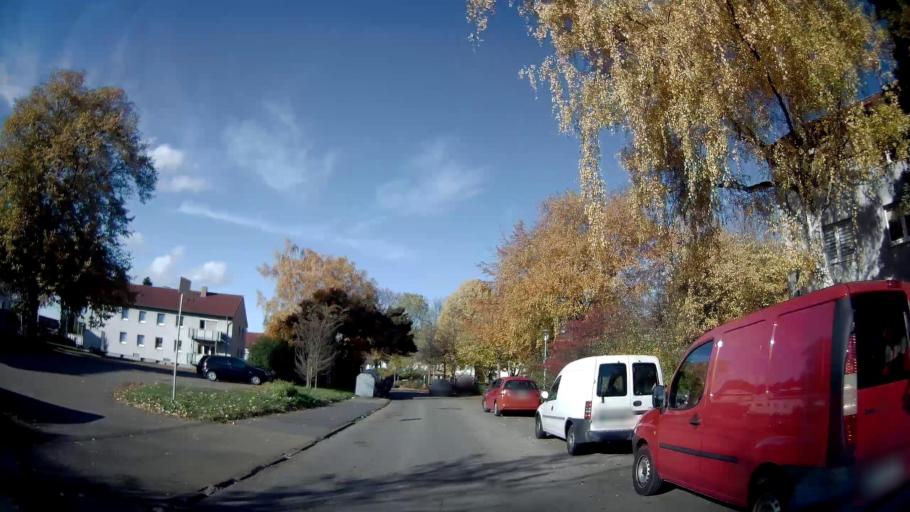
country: DE
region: North Rhine-Westphalia
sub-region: Regierungsbezirk Munster
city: Gladbeck
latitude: 51.5682
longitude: 7.0052
